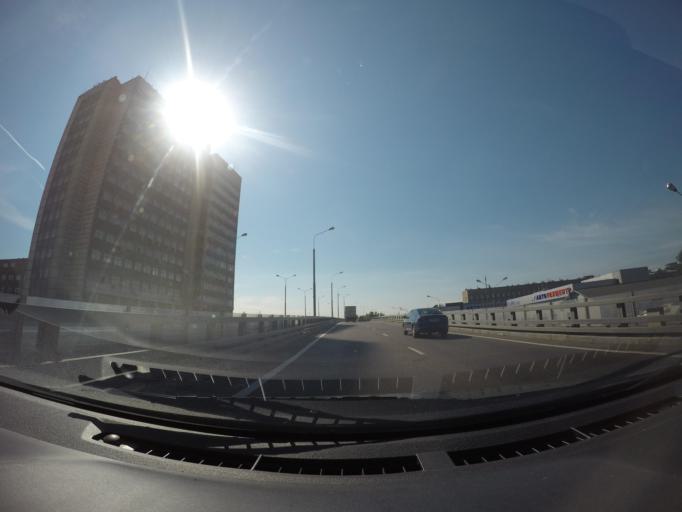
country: RU
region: Moscow
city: Ryazanskiy
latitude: 55.7573
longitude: 37.7396
